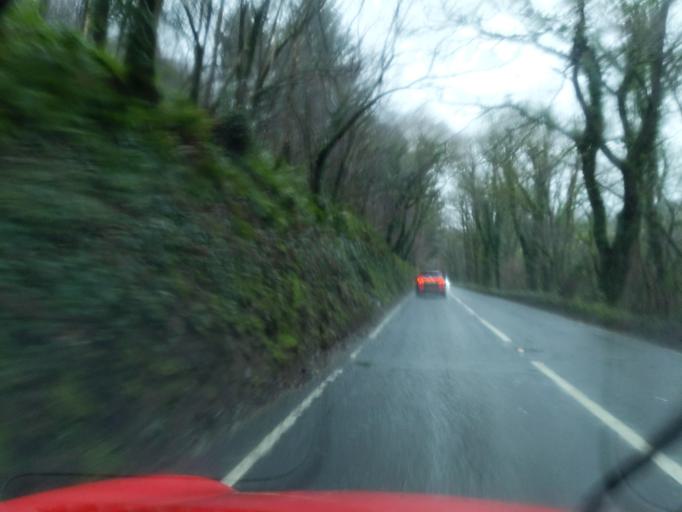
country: GB
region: England
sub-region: Cornwall
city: South Hill
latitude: 50.5598
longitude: -4.3311
